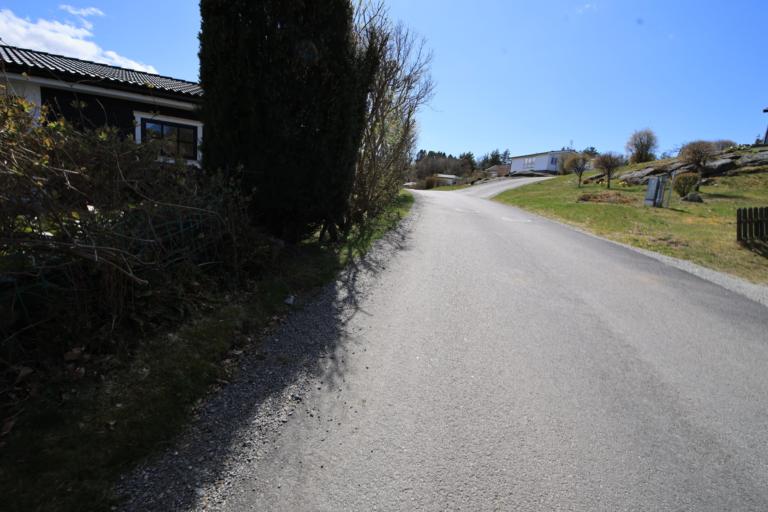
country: SE
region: Halland
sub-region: Varbergs Kommun
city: Varberg
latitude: 57.1824
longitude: 12.2388
